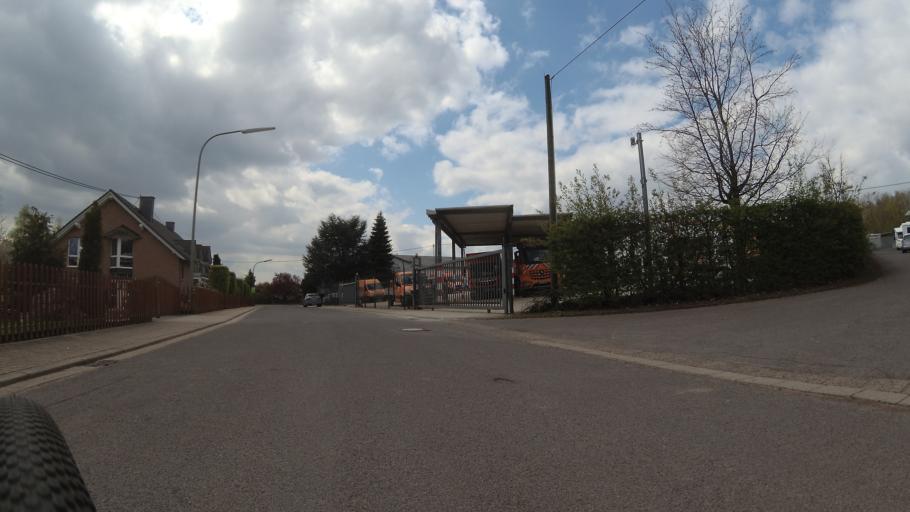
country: DE
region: Saarland
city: Britten
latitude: 49.5278
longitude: 6.6726
